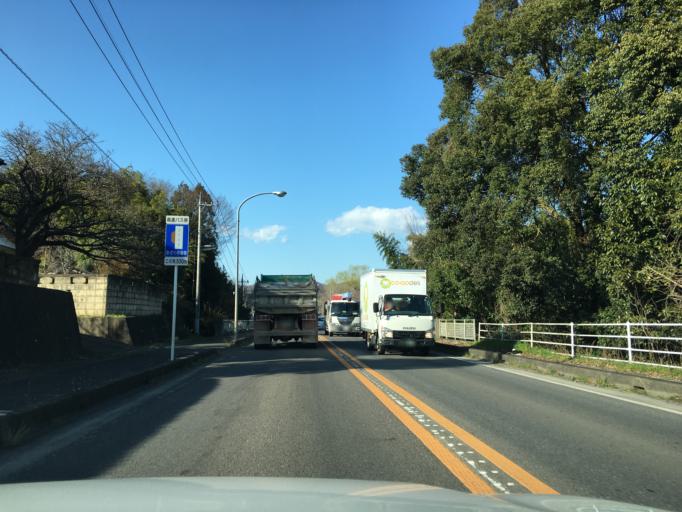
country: JP
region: Ibaraki
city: Omiya
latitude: 36.6212
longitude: 140.4030
